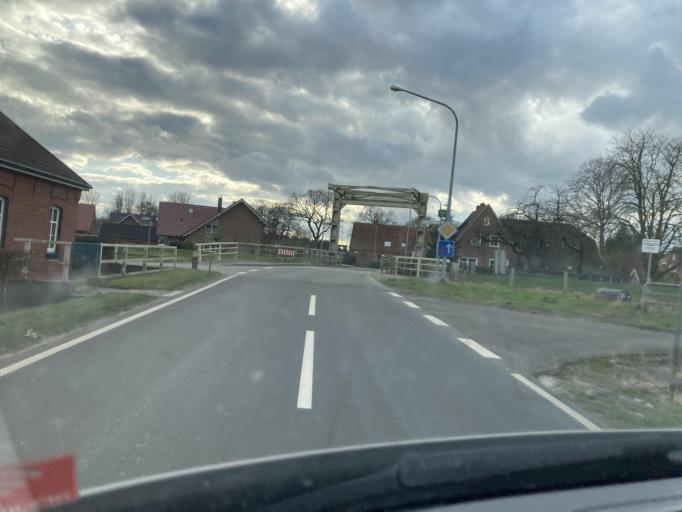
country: DE
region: Lower Saxony
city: Ostrhauderfehn
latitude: 53.1793
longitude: 7.5916
